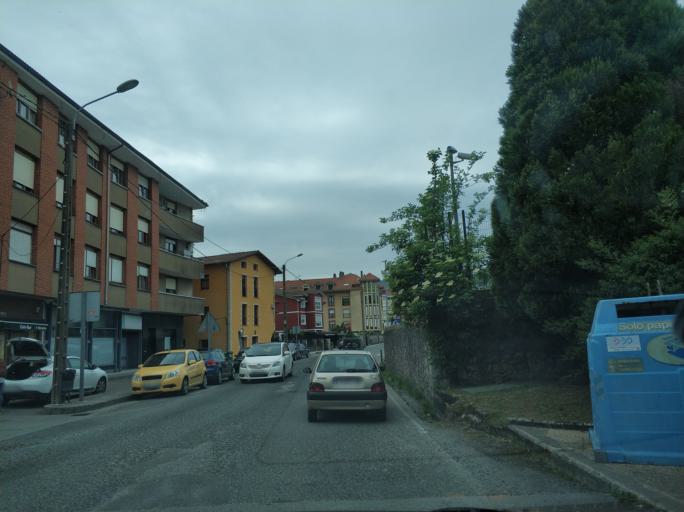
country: ES
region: Cantabria
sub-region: Provincia de Cantabria
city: Santa Maria de Cayon
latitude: 43.3175
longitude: -3.8805
